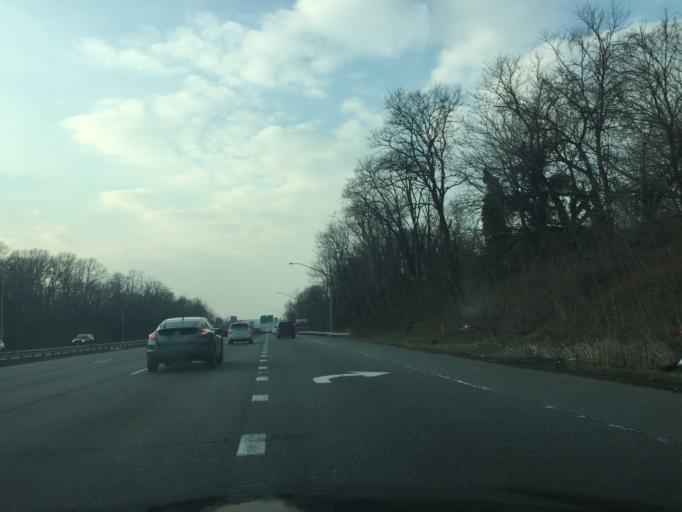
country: US
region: Maryland
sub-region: Anne Arundel County
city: Linthicum
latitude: 39.2130
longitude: -76.6529
